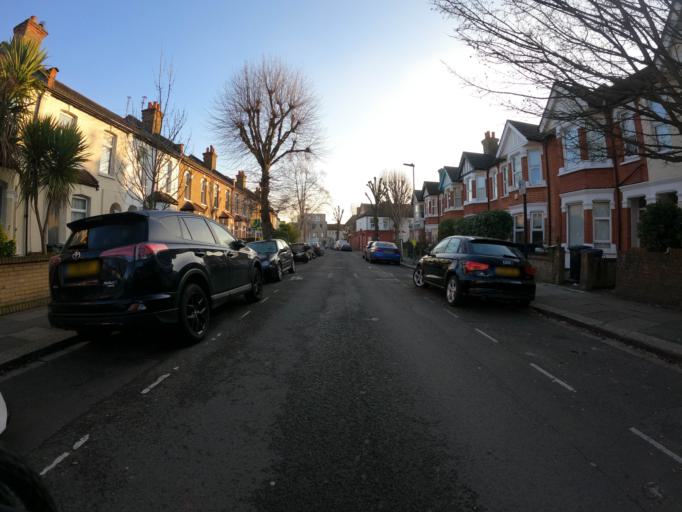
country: GB
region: England
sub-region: Greater London
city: Ealing
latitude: 51.5070
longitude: -0.3204
